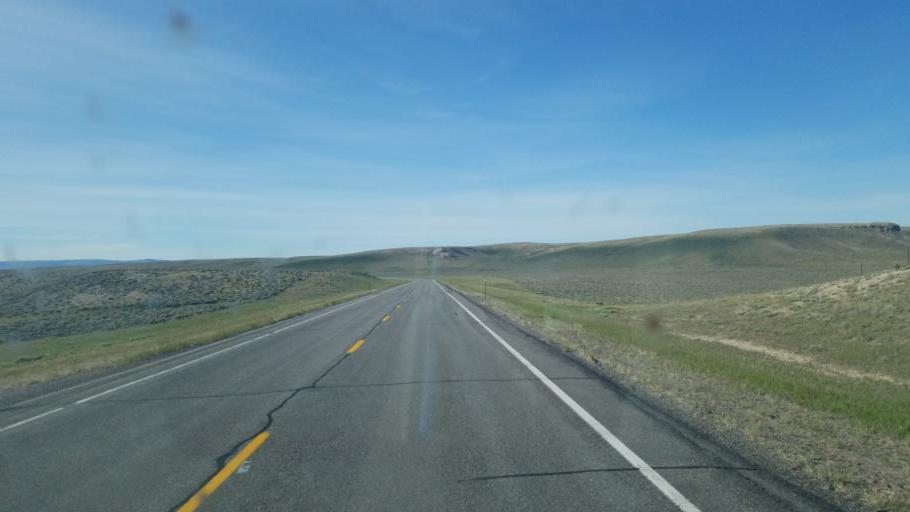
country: US
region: Wyoming
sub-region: Fremont County
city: Riverton
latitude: 42.6235
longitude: -108.1960
